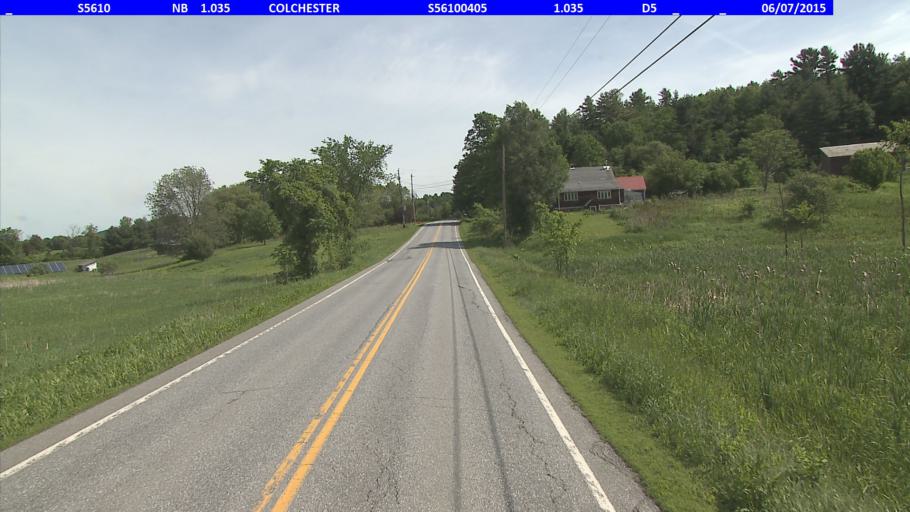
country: US
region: Vermont
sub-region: Chittenden County
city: Colchester
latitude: 44.5562
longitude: -73.1375
